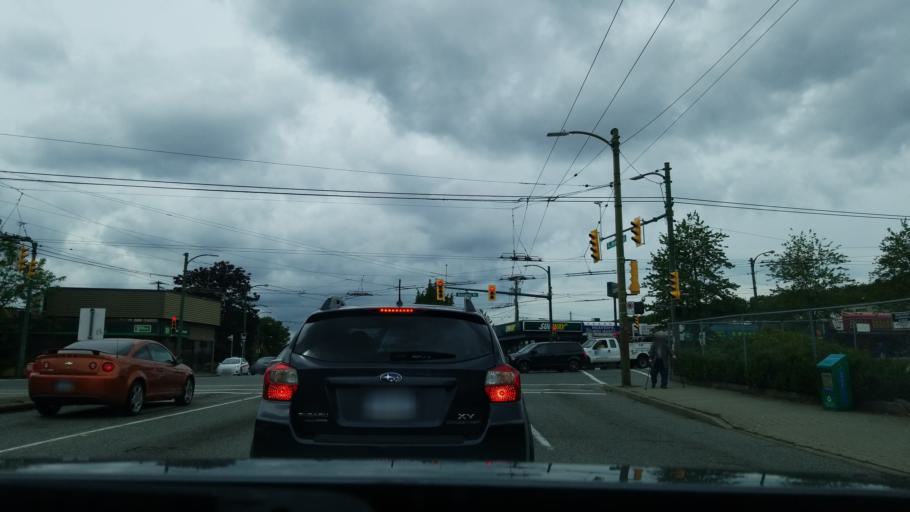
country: CA
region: British Columbia
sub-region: Fraser Valley Regional District
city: North Vancouver
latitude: 49.2621
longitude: -123.0561
